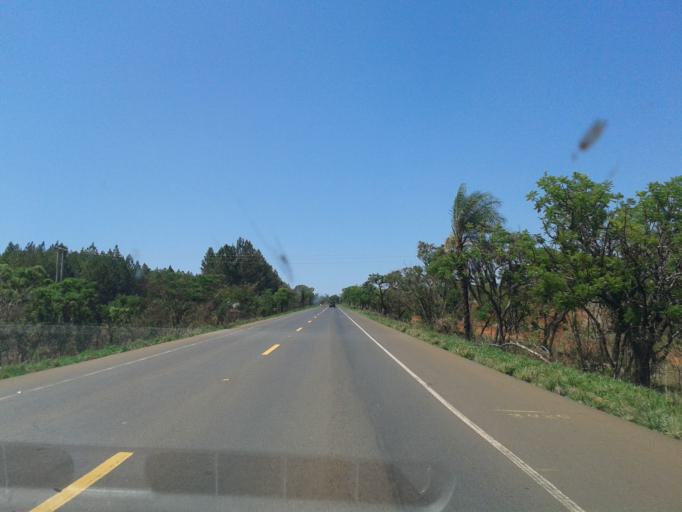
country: BR
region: Minas Gerais
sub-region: Araxa
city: Araxa
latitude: -19.3783
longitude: -47.3496
